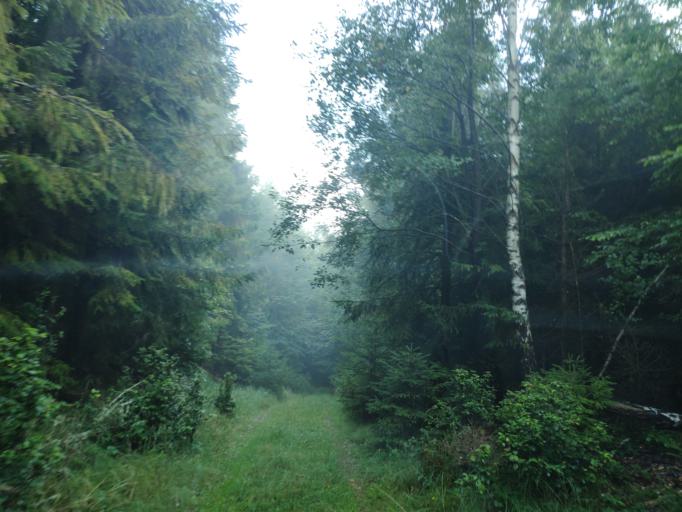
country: SK
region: Kosicky
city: Medzev
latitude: 48.7473
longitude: 20.9863
